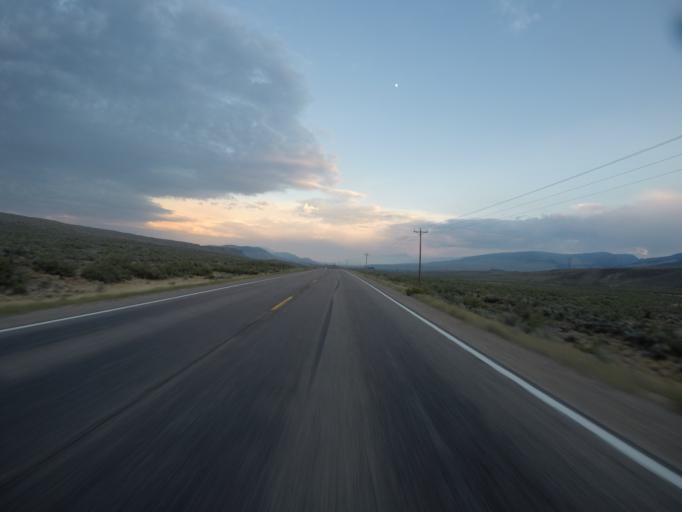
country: US
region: Colorado
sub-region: Grand County
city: Kremmling
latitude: 40.0807
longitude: -106.4144
